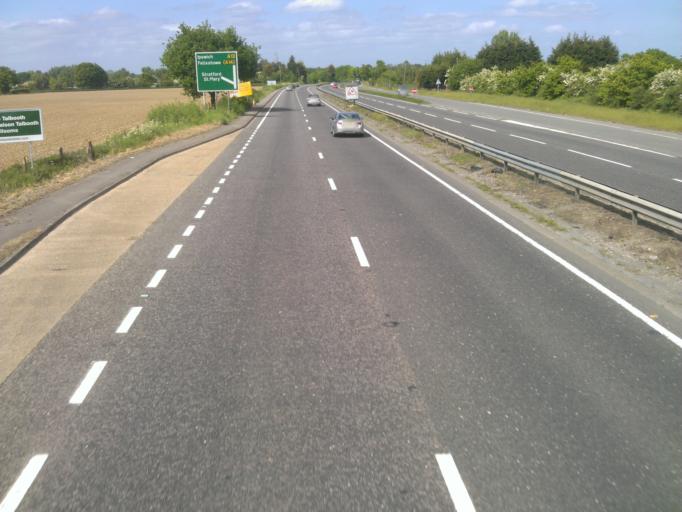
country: GB
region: England
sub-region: Suffolk
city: East Bergholt
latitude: 51.9487
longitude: 0.9591
